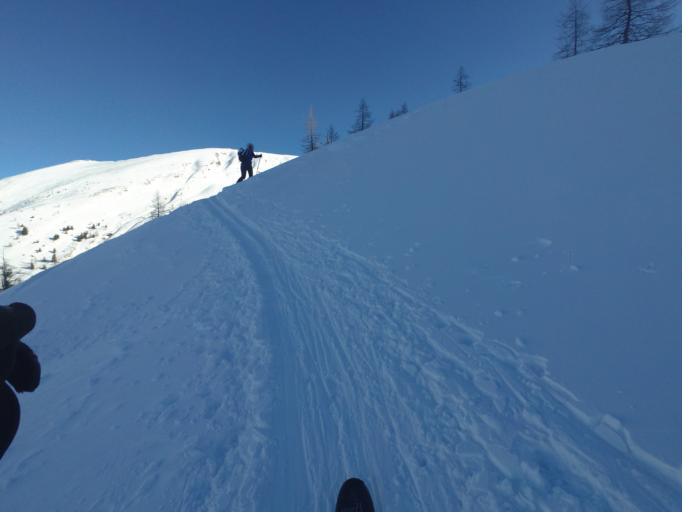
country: AT
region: Salzburg
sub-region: Politischer Bezirk Sankt Johann im Pongau
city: Huttschlag
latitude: 47.1761
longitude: 13.2992
